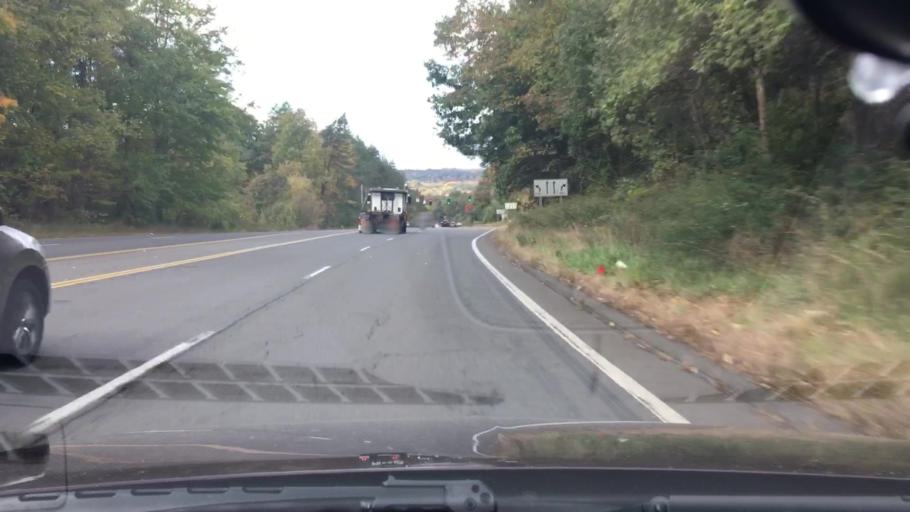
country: US
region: Connecticut
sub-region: New Haven County
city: Wallingford
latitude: 41.4820
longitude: -72.7996
